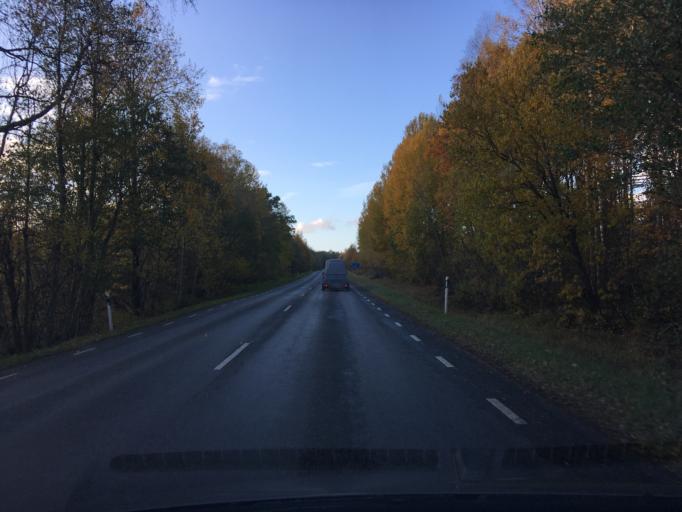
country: EE
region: Paernumaa
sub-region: Audru vald
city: Audru
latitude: 58.5081
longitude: 24.1078
